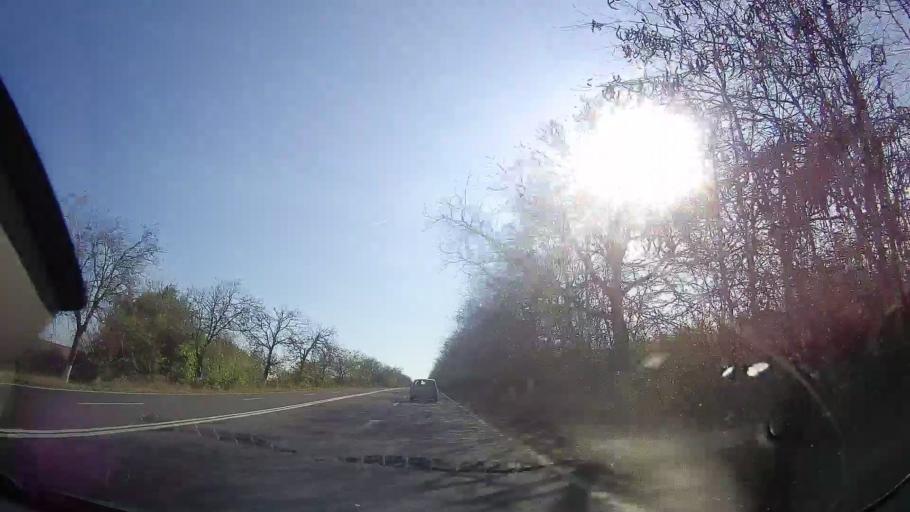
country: RO
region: Constanta
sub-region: Comuna Douazeci si Trei August
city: Douazeci si Trei August
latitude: 43.8940
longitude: 28.5718
